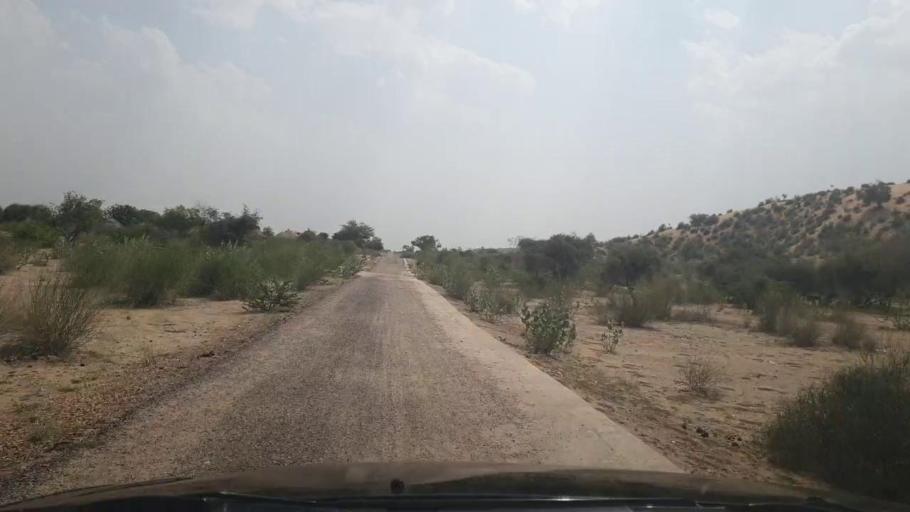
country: PK
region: Sindh
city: Islamkot
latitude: 25.0125
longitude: 70.5265
